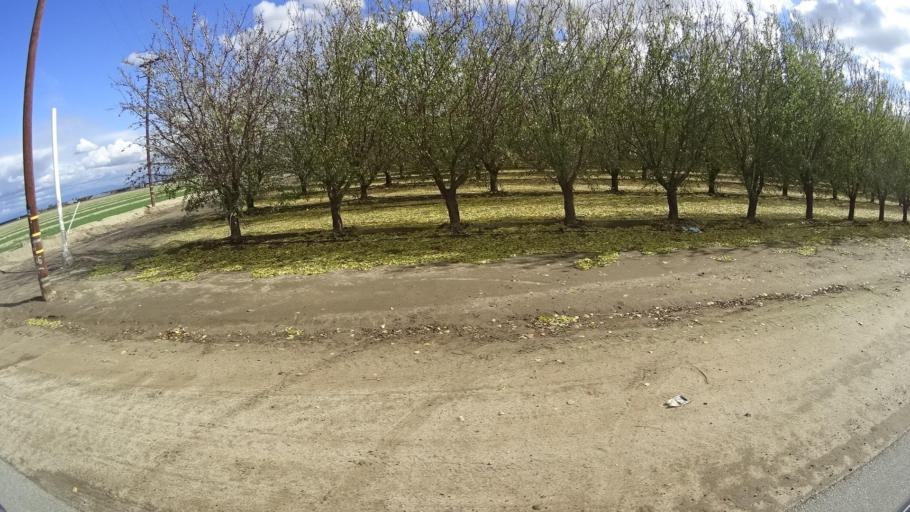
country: US
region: California
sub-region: Kern County
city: Greenfield
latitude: 35.2304
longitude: -119.0745
